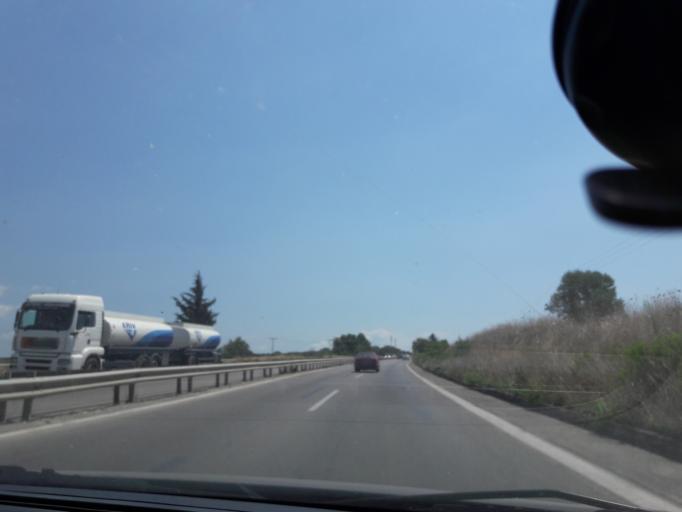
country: GR
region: Central Macedonia
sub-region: Nomos Chalkidikis
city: Nea Kallikrateia
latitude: 40.3046
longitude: 23.1313
